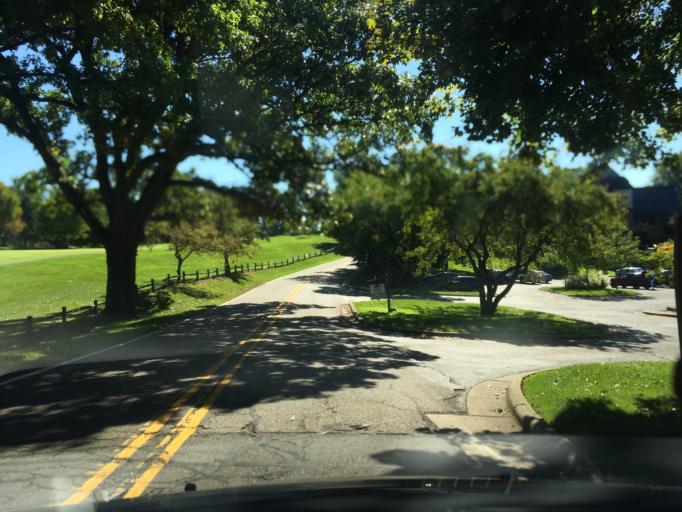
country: US
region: Michigan
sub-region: Oakland County
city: Sylvan Lake
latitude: 42.5986
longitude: -83.2981
